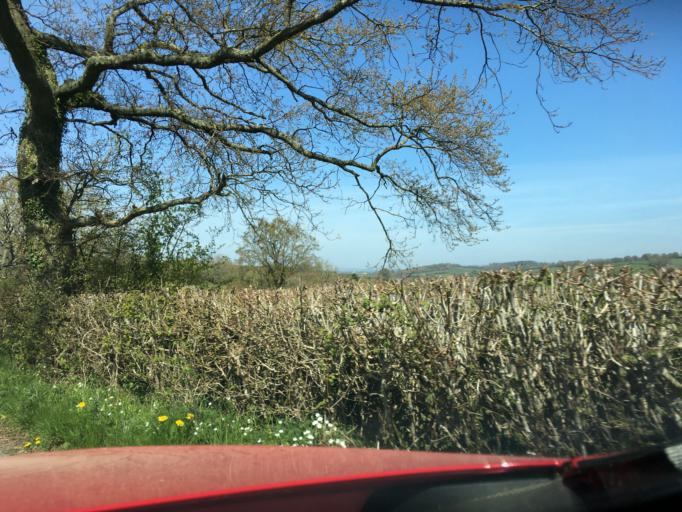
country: GB
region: Wales
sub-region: Monmouthshire
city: Llangwm
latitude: 51.7395
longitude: -2.8238
